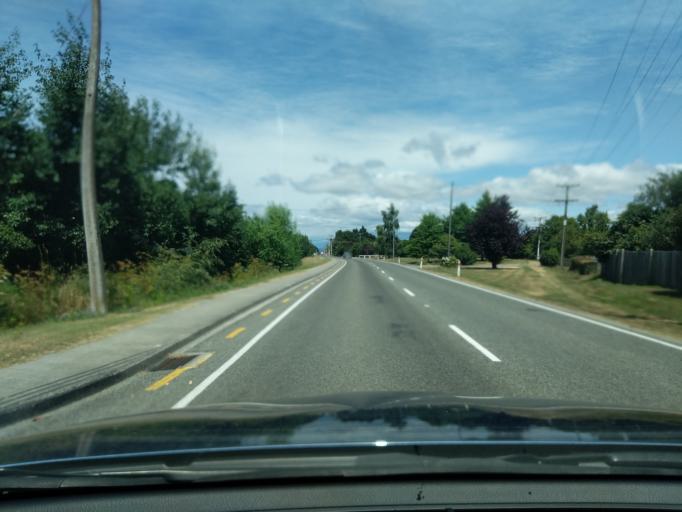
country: NZ
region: Tasman
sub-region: Tasman District
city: Motueka
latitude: -41.0804
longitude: 172.9972
